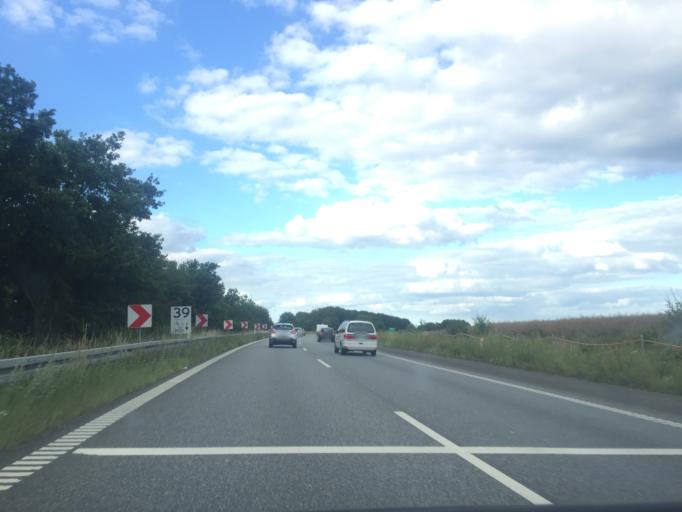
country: DK
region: Zealand
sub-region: Koge Kommune
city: Ejby
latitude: 55.4761
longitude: 12.1307
